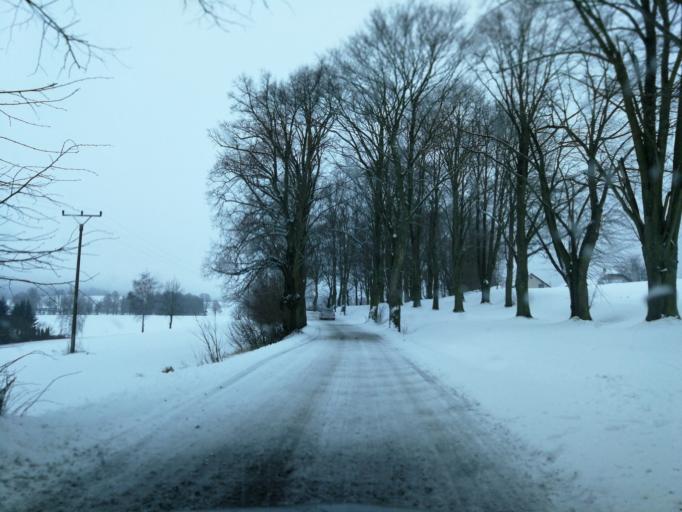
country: CZ
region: Vysocina
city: Heralec
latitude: 49.5283
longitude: 15.4681
